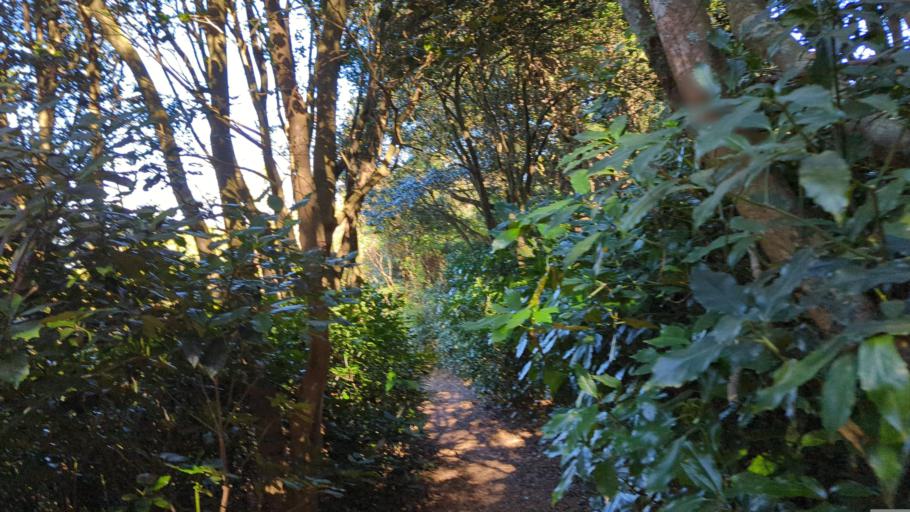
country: JP
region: Shizuoka
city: Kosai-shi
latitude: 34.7778
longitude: 137.4782
